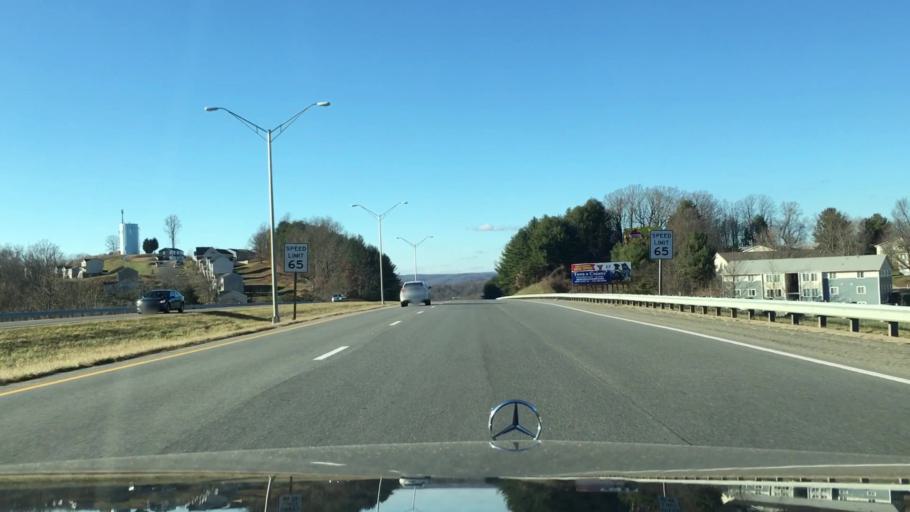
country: US
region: Virginia
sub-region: Montgomery County
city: Christiansburg
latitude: 37.1371
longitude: -80.3786
